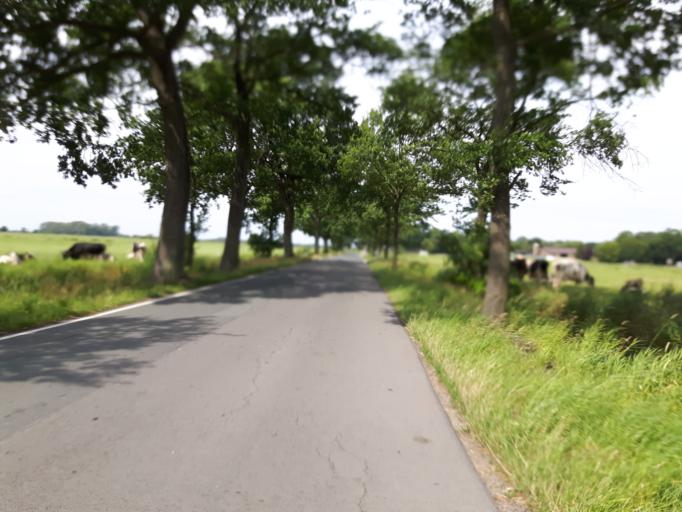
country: DE
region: Lower Saxony
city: Rastede
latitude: 53.3277
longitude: 8.2696
